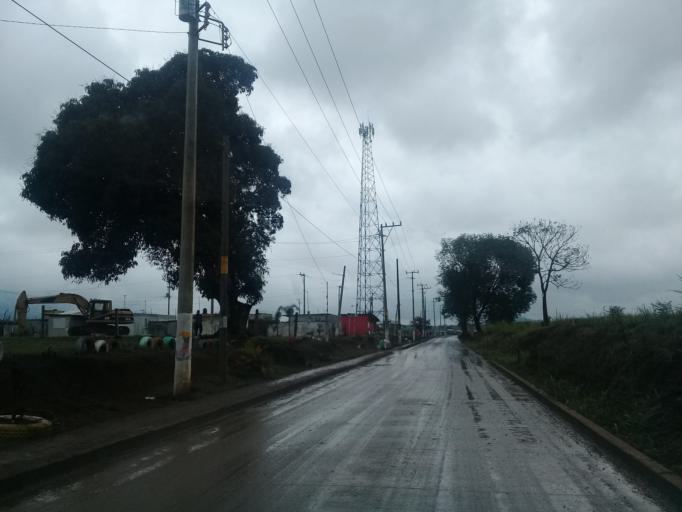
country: MX
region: Veracruz
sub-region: Cordoba
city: San Jose de Tapia
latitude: 18.8519
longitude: -96.9570
